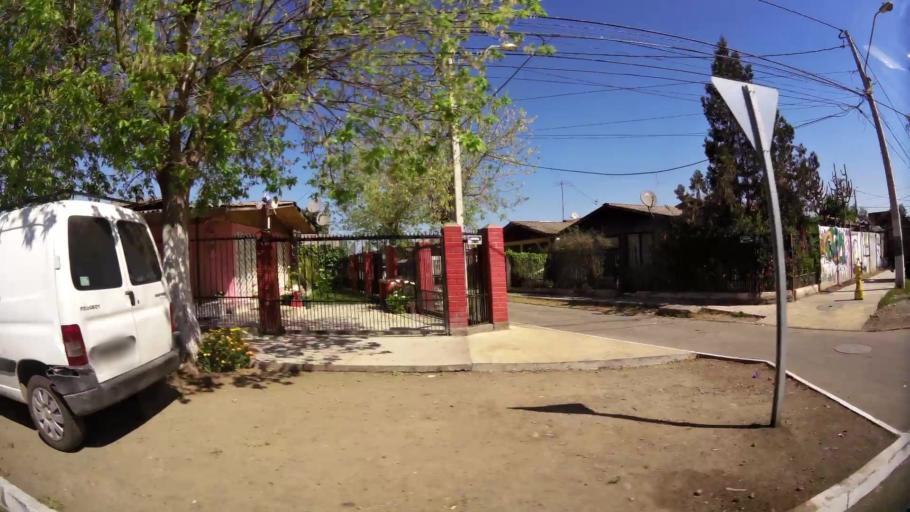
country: CL
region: Santiago Metropolitan
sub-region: Provincia de Talagante
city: Penaflor
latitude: -33.6040
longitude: -70.8786
